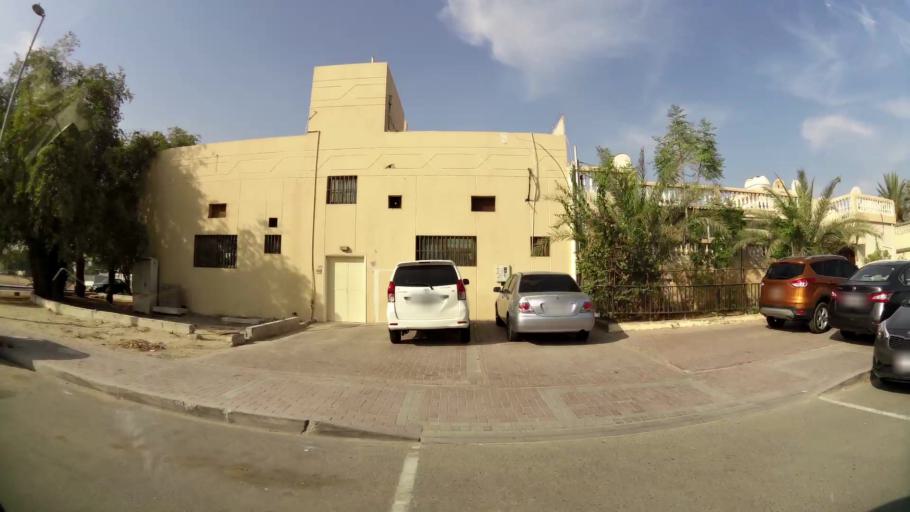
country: AE
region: Ash Shariqah
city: Sharjah
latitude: 25.2256
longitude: 55.3825
